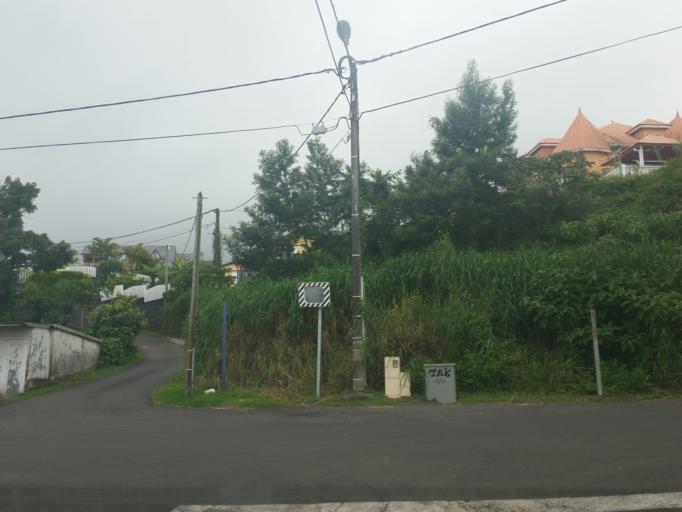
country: RE
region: Reunion
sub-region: Reunion
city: Le Tampon
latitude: -21.2346
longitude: 55.5222
